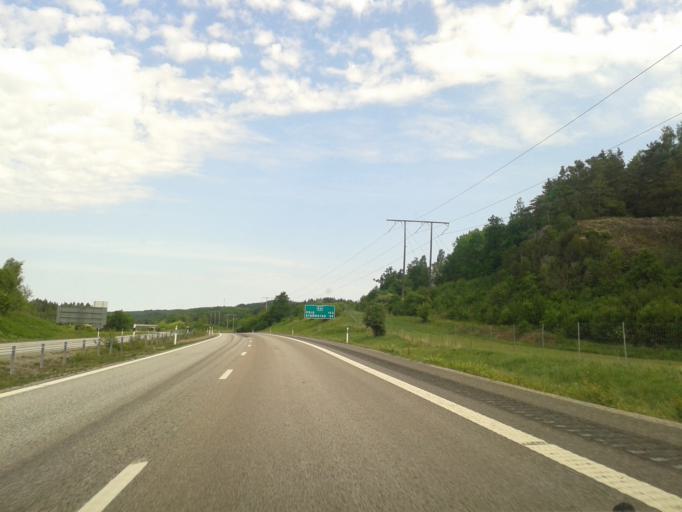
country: SE
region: Vaestra Goetaland
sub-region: Munkedals Kommun
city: Munkedal
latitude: 58.5255
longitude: 11.5454
